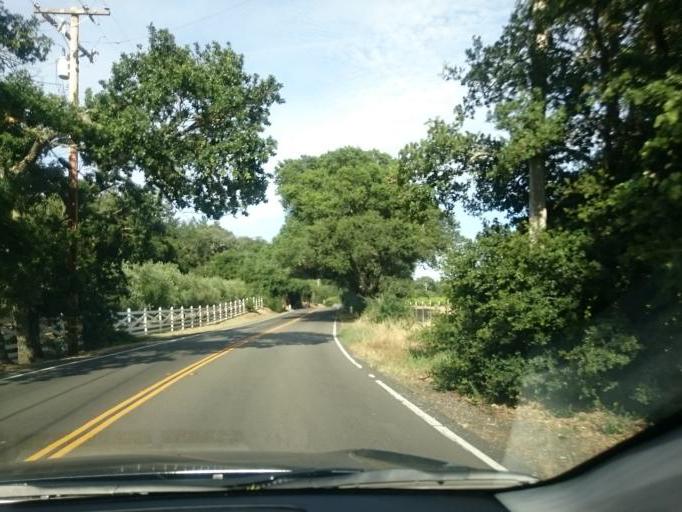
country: US
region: California
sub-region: Napa County
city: Calistoga
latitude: 38.6028
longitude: -122.6311
